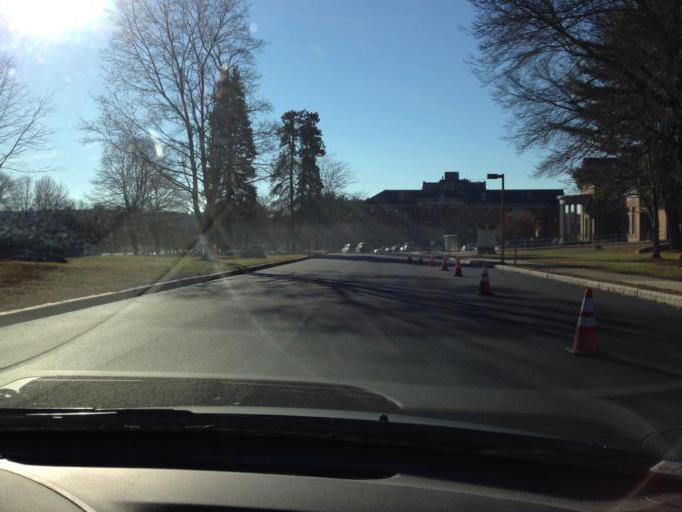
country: US
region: Massachusetts
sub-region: Middlesex County
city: Bedford
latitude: 42.5065
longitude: -71.2733
